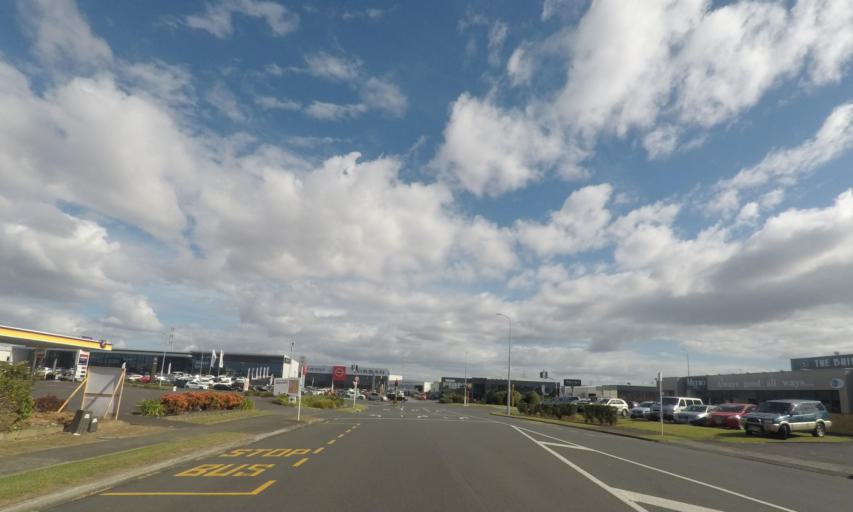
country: NZ
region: Auckland
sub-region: Auckland
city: Pakuranga
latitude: -36.9257
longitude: 174.8947
